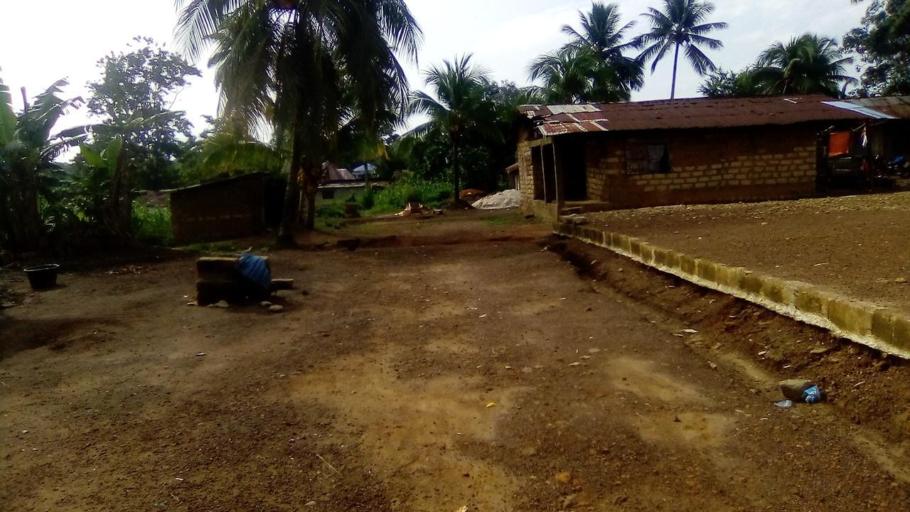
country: SL
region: Southern Province
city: Pujehun
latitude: 7.3597
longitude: -11.7215
